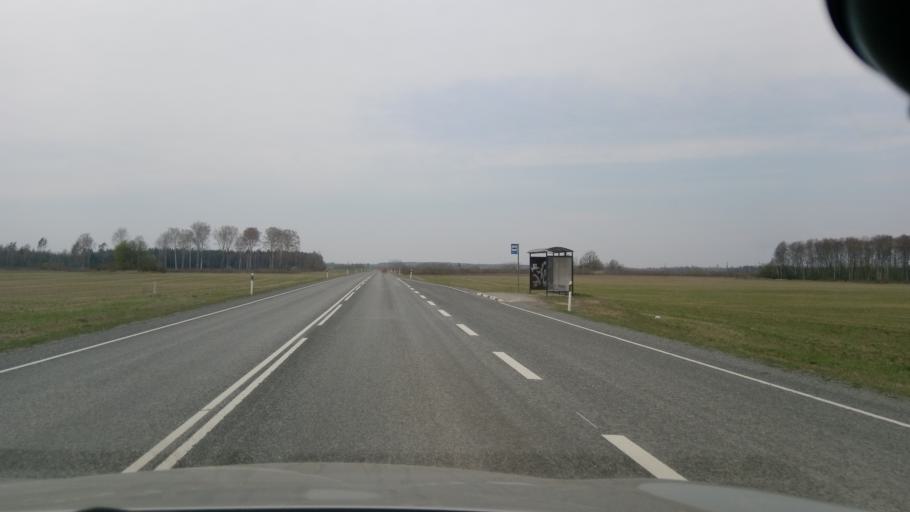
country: EE
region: Jaervamaa
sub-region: Tueri vald
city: Sarevere
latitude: 58.7716
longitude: 25.5195
